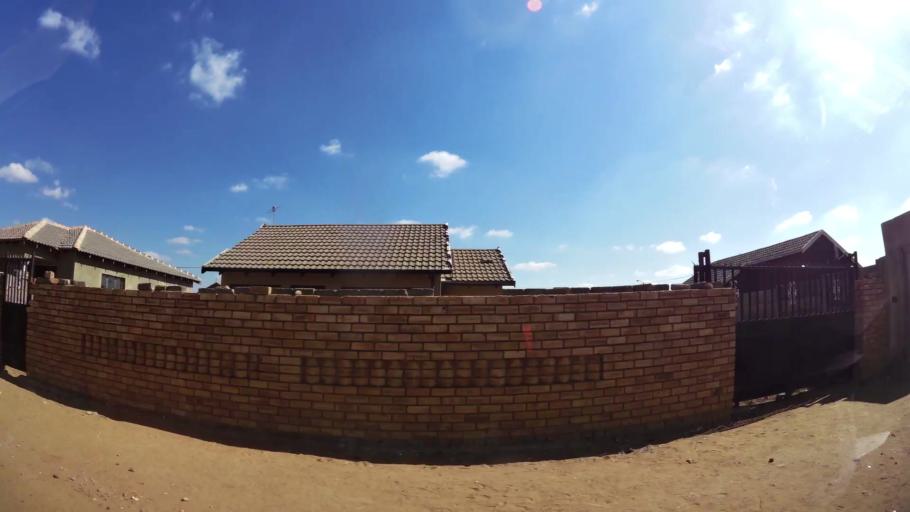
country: ZA
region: Gauteng
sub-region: West Rand District Municipality
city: Krugersdorp
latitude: -26.1482
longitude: 27.7731
